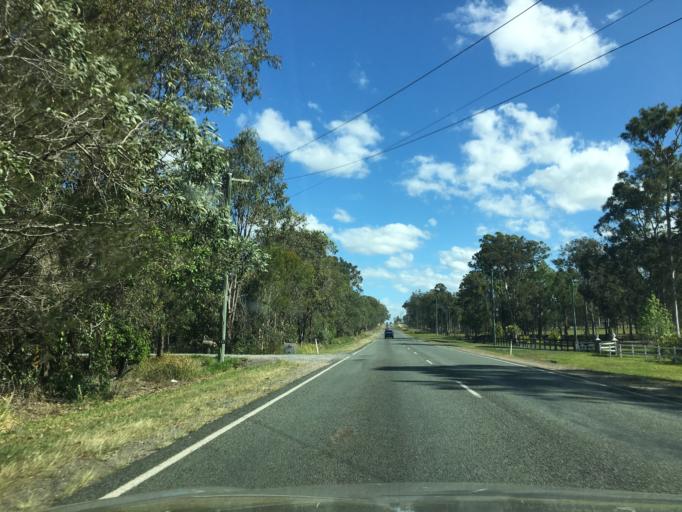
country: AU
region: Queensland
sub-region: Logan
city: Logan Reserve
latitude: -27.7350
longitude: 153.1284
